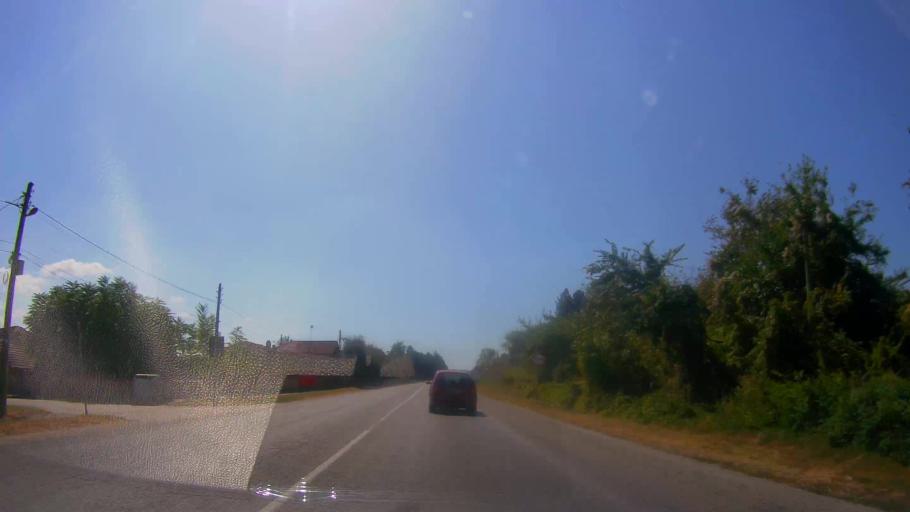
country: BG
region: Veliko Turnovo
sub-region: Obshtina Polski Trumbesh
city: Polski Trumbesh
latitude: 43.2675
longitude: 25.6436
